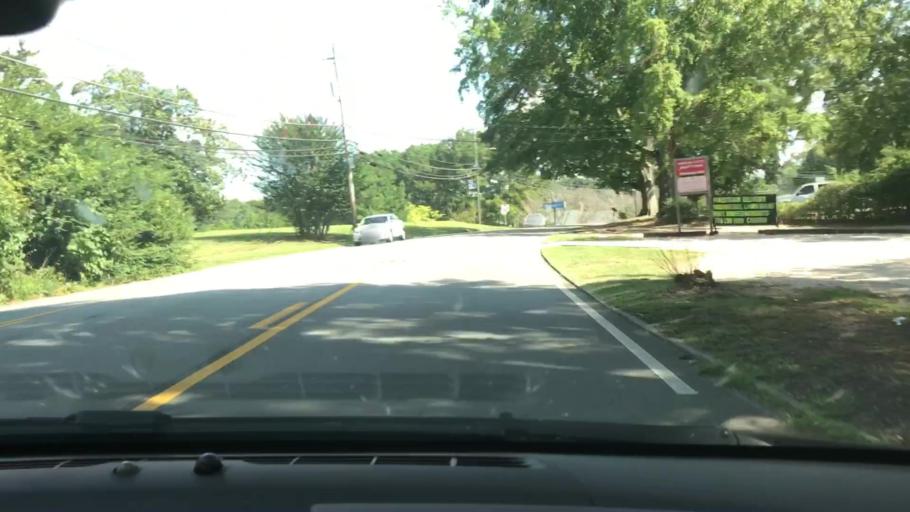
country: US
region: Georgia
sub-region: Troup County
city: La Grange
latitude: 33.0602
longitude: -85.0353
